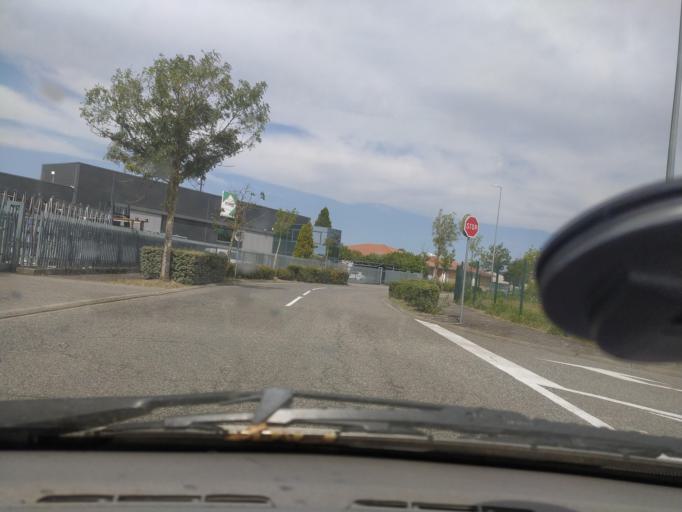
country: FR
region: Midi-Pyrenees
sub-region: Departement de la Haute-Garonne
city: Tournefeuille
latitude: 43.5928
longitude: 1.3134
